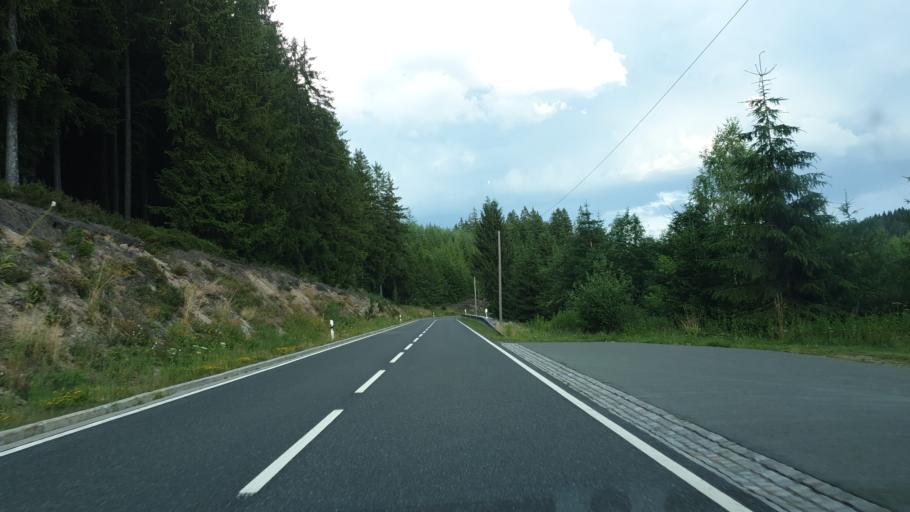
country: DE
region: Saxony
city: Tannenbergsthal
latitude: 50.4537
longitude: 12.4511
